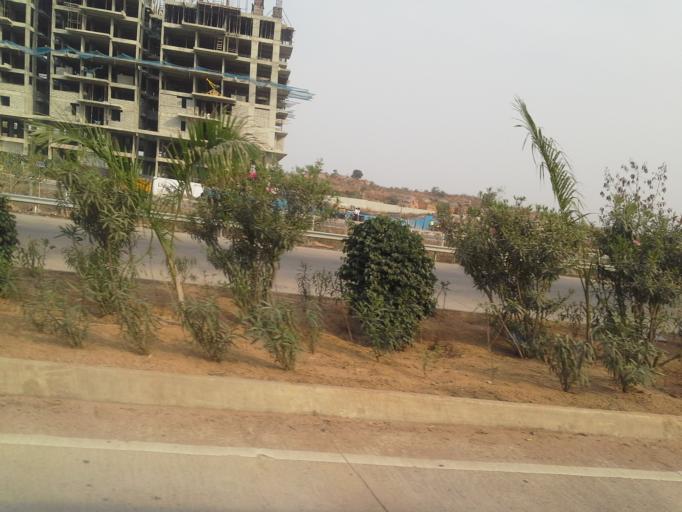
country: IN
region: Telangana
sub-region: Rangareddi
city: Kukatpalli
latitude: 17.4052
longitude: 78.3534
